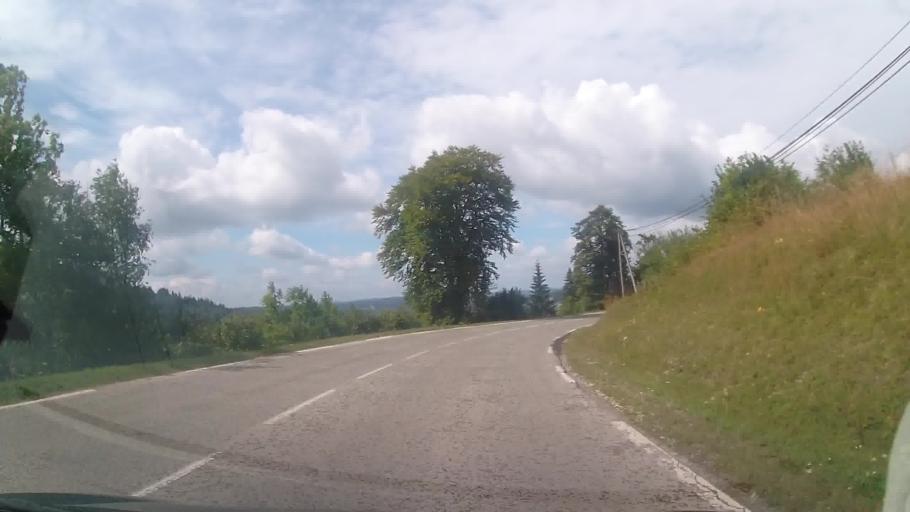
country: FR
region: Franche-Comte
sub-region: Departement du Jura
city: Les Rousses
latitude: 46.4519
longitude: 6.0710
